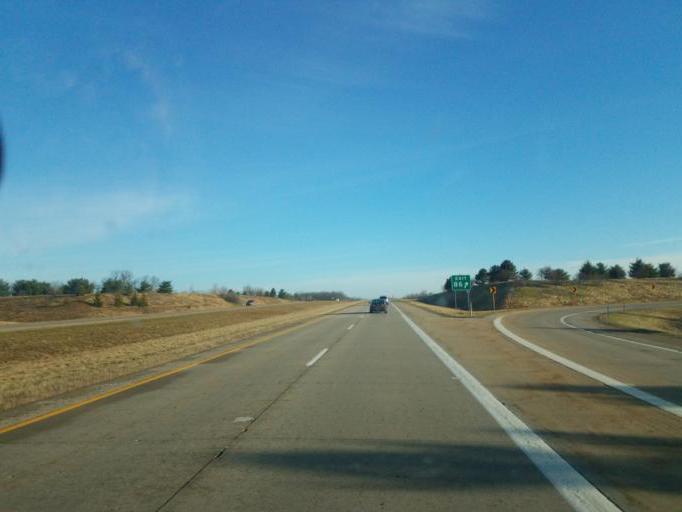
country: US
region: Michigan
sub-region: Clinton County
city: DeWitt
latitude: 42.8570
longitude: -84.5185
